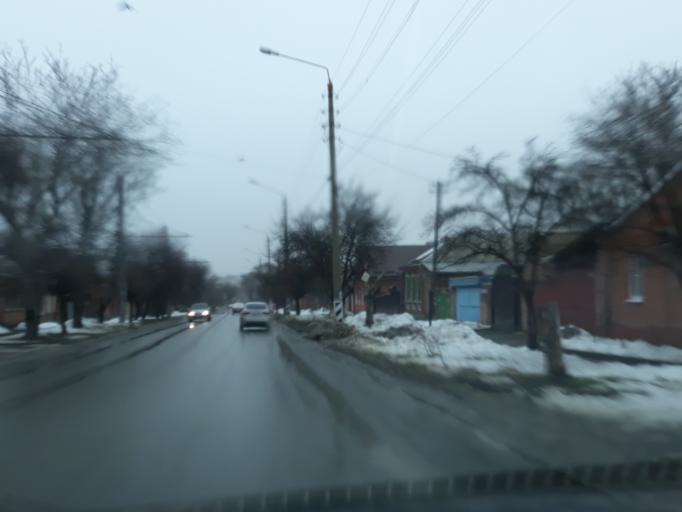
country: RU
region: Rostov
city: Taganrog
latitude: 47.2198
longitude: 38.9036
